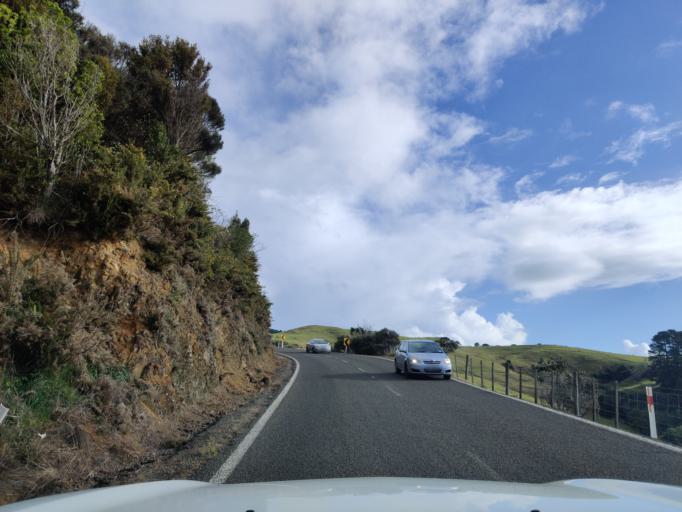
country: NZ
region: Waikato
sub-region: Thames-Coromandel District
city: Coromandel
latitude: -36.8145
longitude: 175.4877
